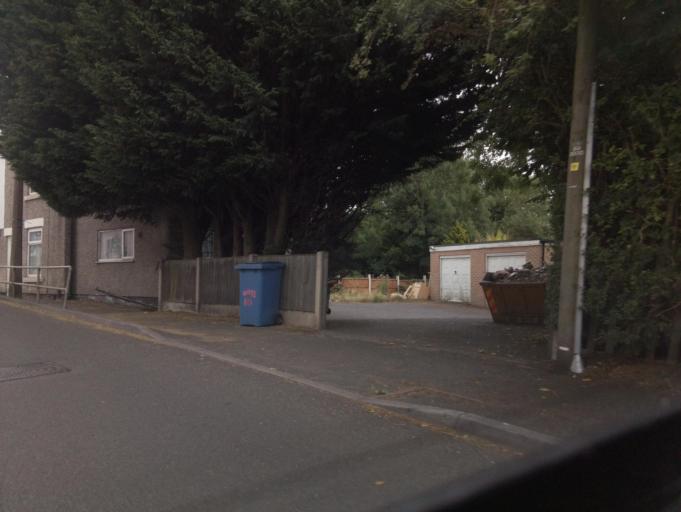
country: GB
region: England
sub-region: Derbyshire
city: Borrowash
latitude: 52.9046
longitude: -1.3739
